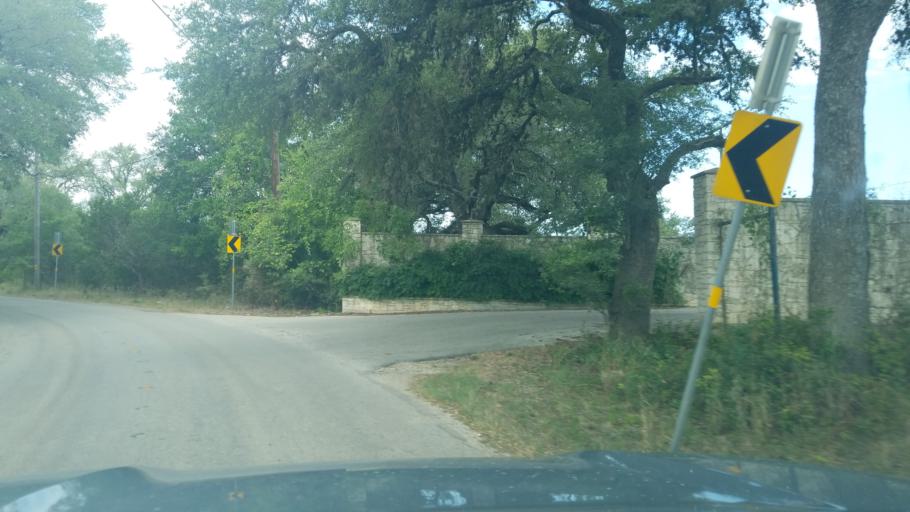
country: US
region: Texas
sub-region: Comal County
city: Bulverde
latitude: 29.7595
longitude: -98.4105
